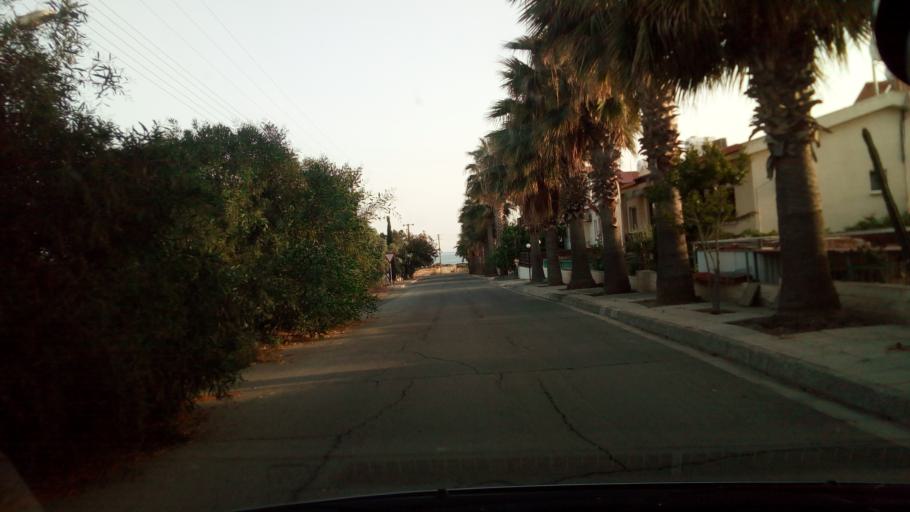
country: CY
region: Larnaka
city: Kofinou
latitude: 34.7338
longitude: 33.3535
